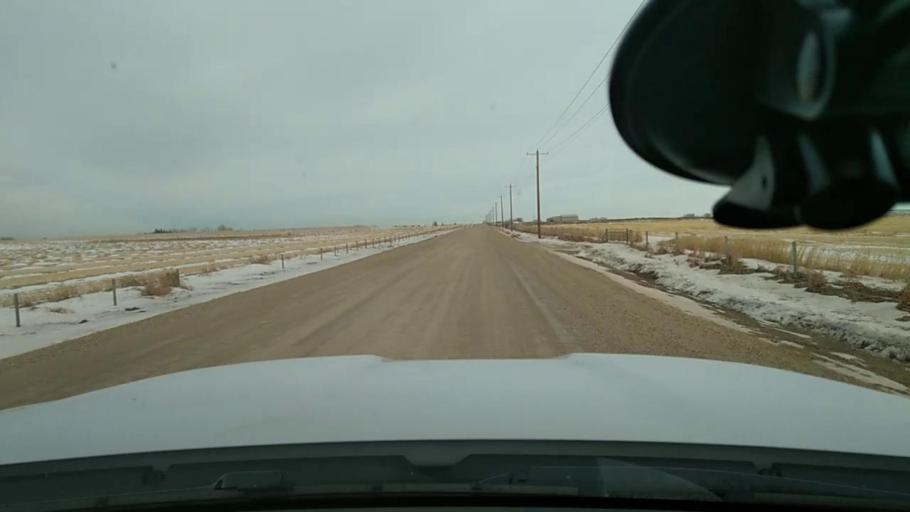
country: CA
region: Alberta
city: Airdrie
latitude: 51.2176
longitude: -113.9118
